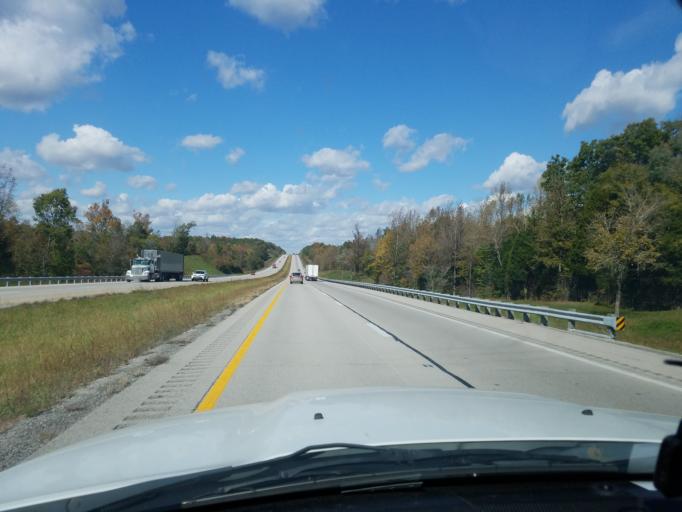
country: US
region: Kentucky
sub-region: Ohio County
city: Hartford
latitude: 37.5702
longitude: -86.9496
